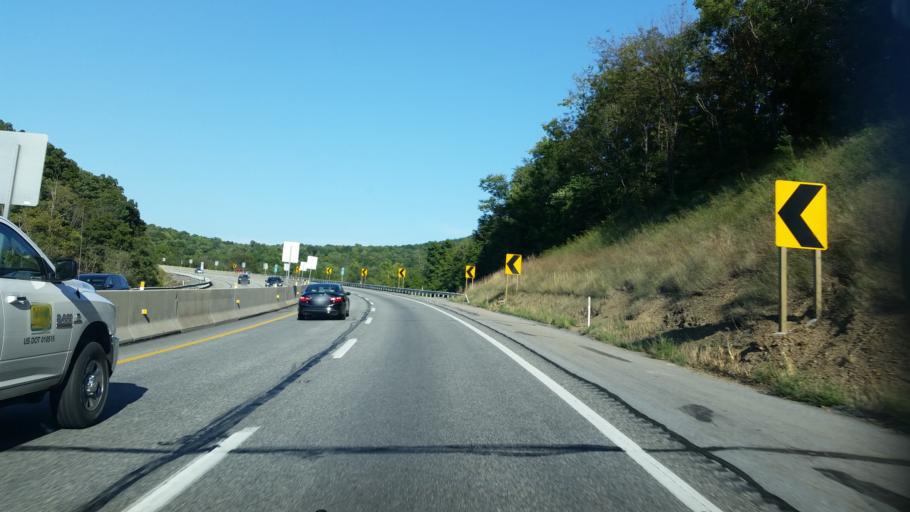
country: US
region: Pennsylvania
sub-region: Fulton County
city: McConnellsburg
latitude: 40.0669
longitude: -77.9237
